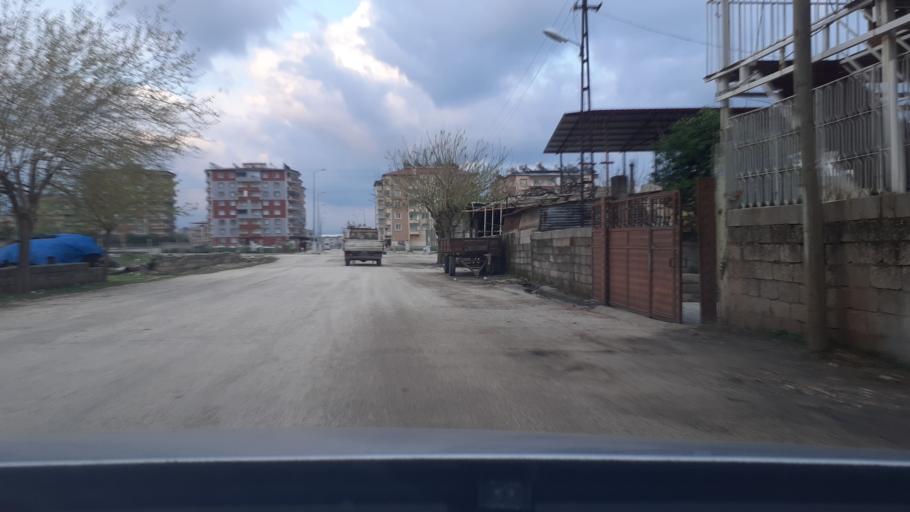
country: TR
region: Hatay
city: Kirikhan
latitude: 36.4833
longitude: 36.3513
